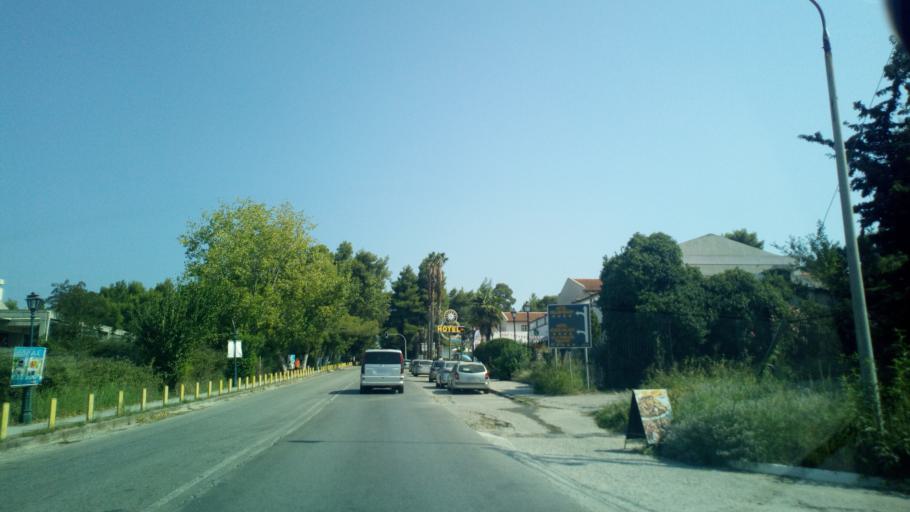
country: GR
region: Central Macedonia
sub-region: Nomos Chalkidikis
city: Kallithea
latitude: 40.0613
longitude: 23.4569
